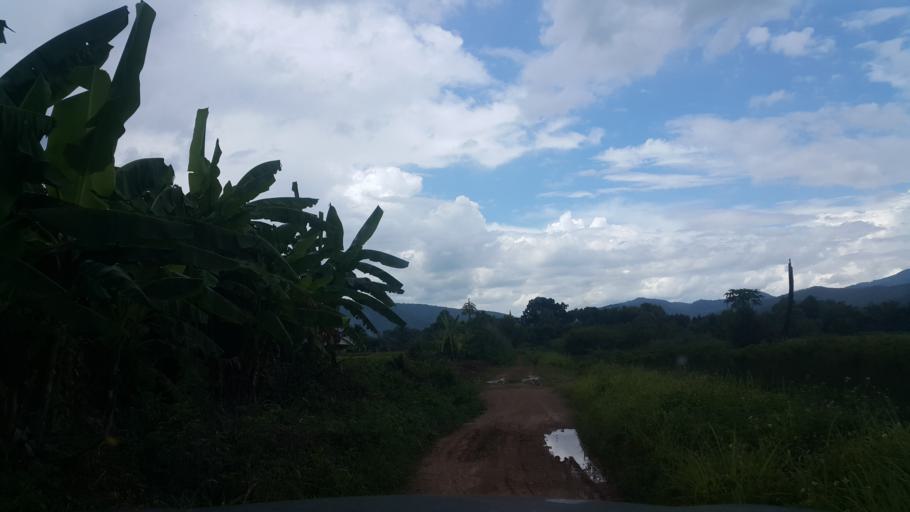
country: TH
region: Chiang Mai
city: Mae Taeng
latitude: 19.1921
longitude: 99.0012
